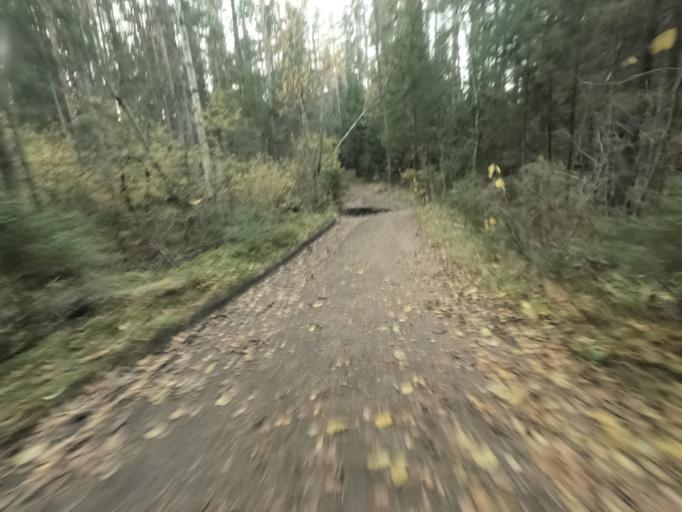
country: RU
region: Leningrad
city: Leninskoye
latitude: 60.1958
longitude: 29.8494
